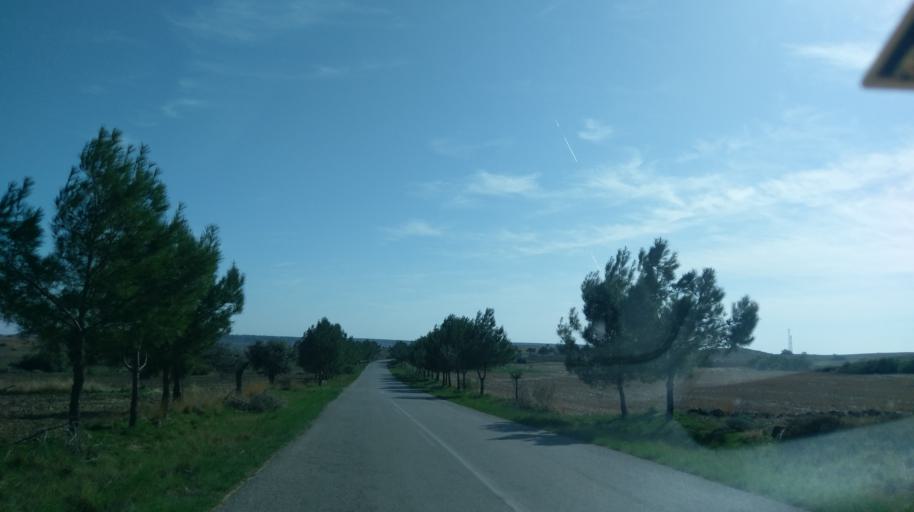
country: CY
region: Ammochostos
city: Trikomo
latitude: 35.3838
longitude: 34.0009
